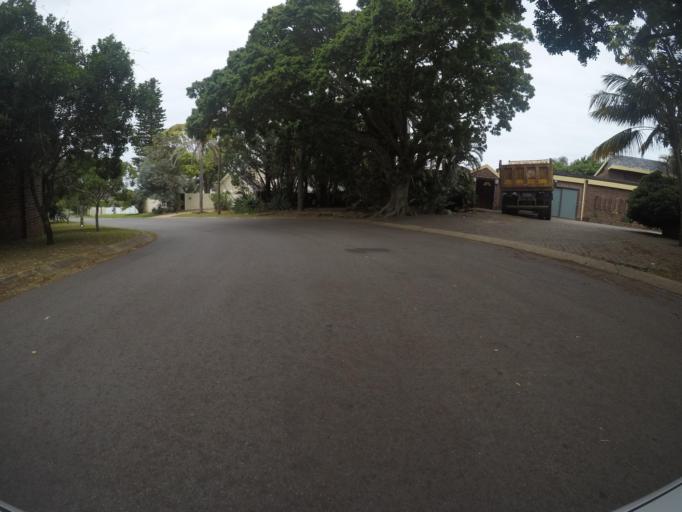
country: ZA
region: Eastern Cape
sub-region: Buffalo City Metropolitan Municipality
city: East London
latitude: -32.9776
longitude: 27.9472
